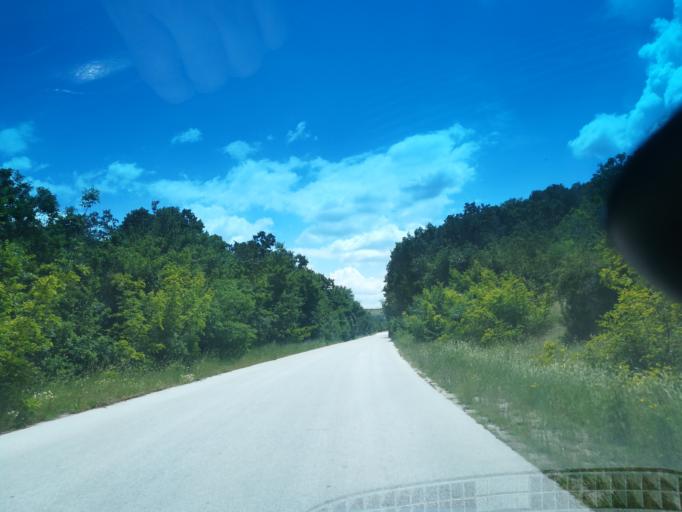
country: BG
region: Khaskovo
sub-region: Obshtina Mineralni Bani
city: Mineralni Bani
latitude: 41.9723
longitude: 25.2600
